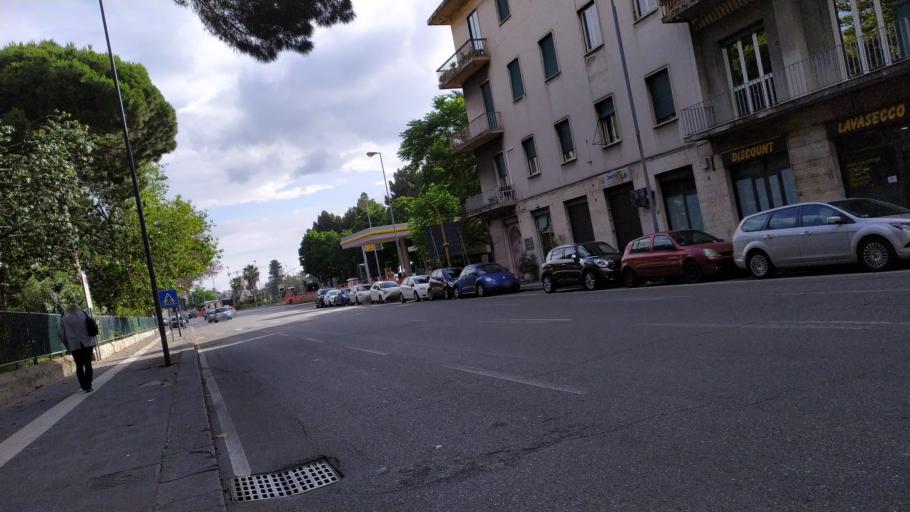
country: IT
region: Sicily
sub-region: Messina
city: Messina
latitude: 38.1980
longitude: 15.5567
